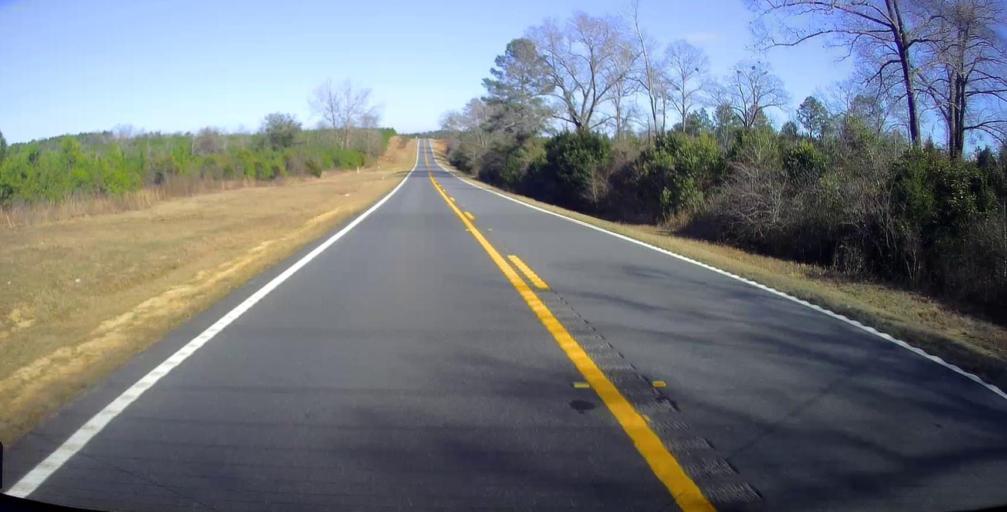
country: US
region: Georgia
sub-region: Taylor County
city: Butler
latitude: 32.4398
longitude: -84.2697
